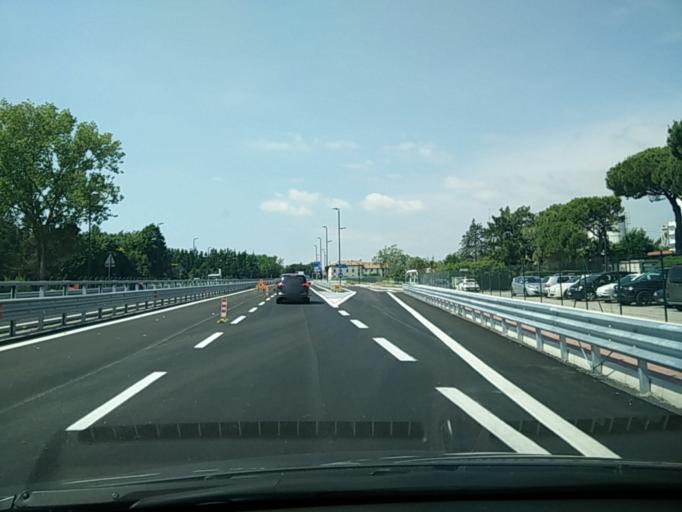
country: IT
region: Veneto
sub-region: Provincia di Venezia
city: Tessera
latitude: 45.5091
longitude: 12.3359
